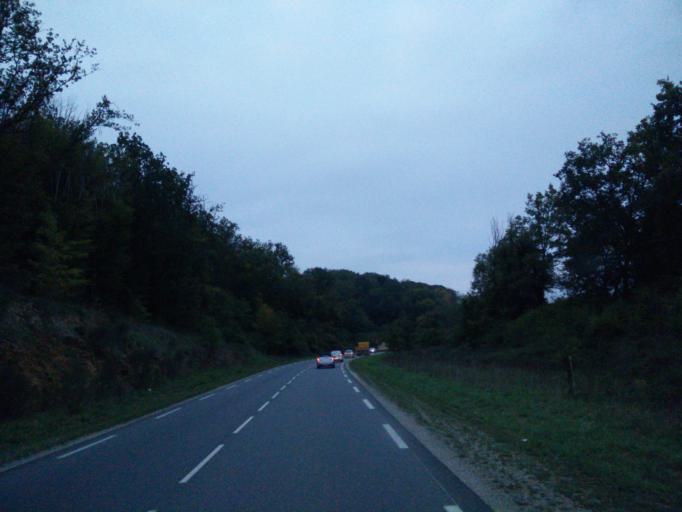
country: FR
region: Aquitaine
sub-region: Departement de la Dordogne
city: Sarlat-la-Caneda
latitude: 44.8879
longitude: 1.2020
